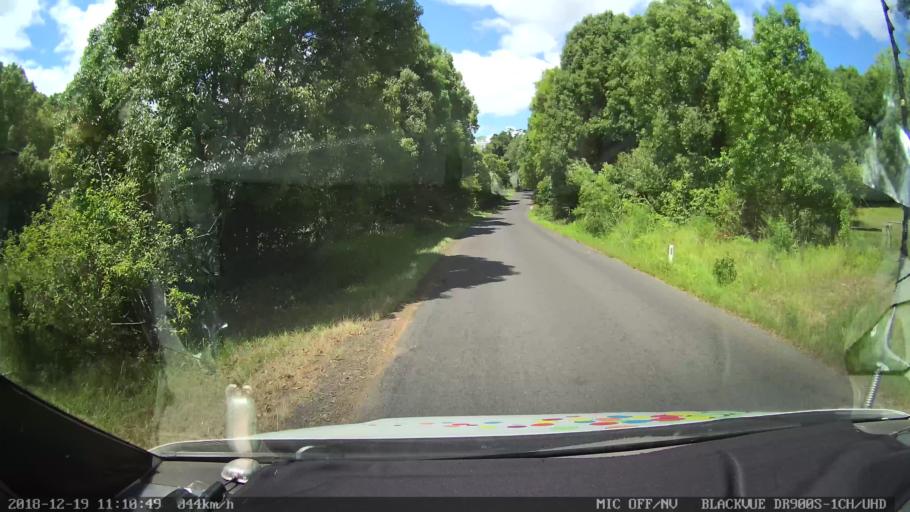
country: AU
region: New South Wales
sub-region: Lismore Municipality
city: Nimbin
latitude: -28.6402
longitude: 153.2598
